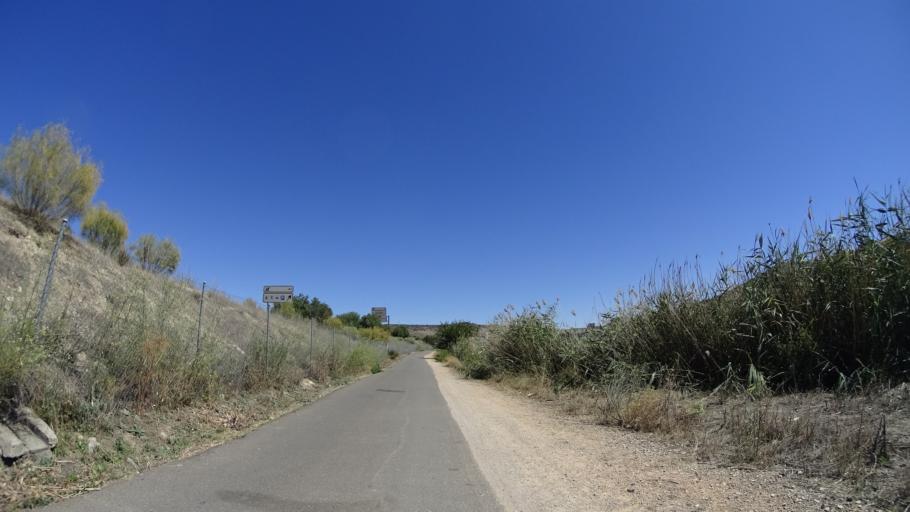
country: ES
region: Madrid
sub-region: Provincia de Madrid
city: Perales de Tajuna
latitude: 40.2276
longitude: -3.3378
